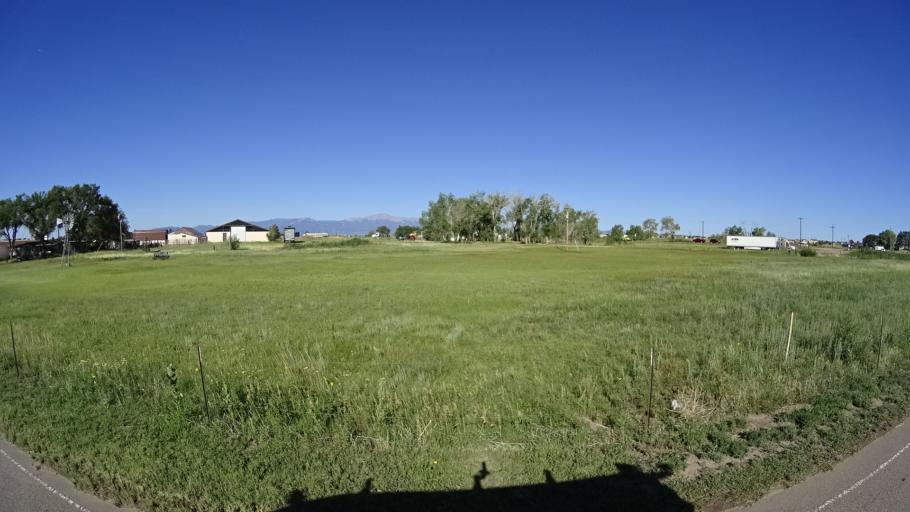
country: US
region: Colorado
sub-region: El Paso County
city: Cimarron Hills
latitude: 38.9314
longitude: -104.6084
